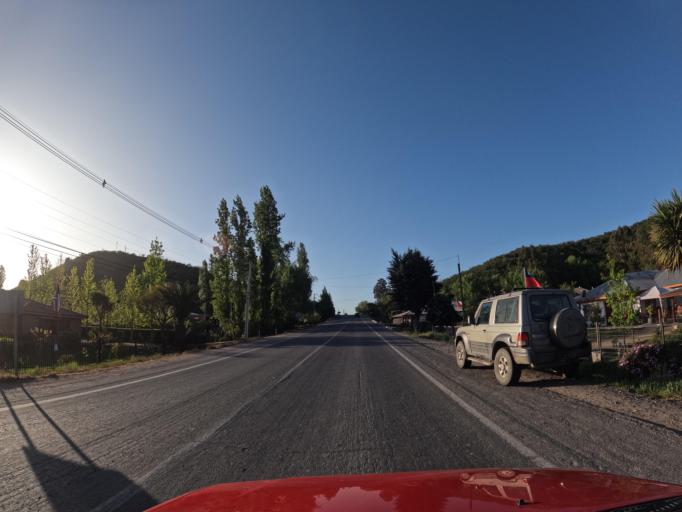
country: CL
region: O'Higgins
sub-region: Provincia de Colchagua
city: Santa Cruz
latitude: -34.4263
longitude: -71.3730
